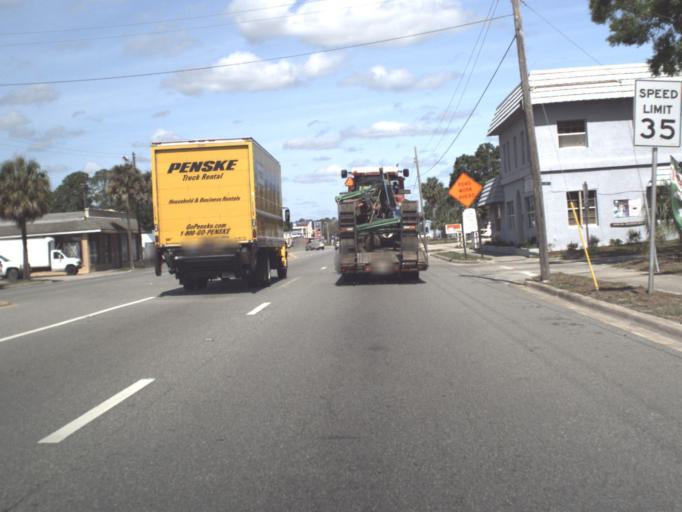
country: US
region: Florida
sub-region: Flagler County
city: Bunnell
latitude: 29.4668
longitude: -81.2591
